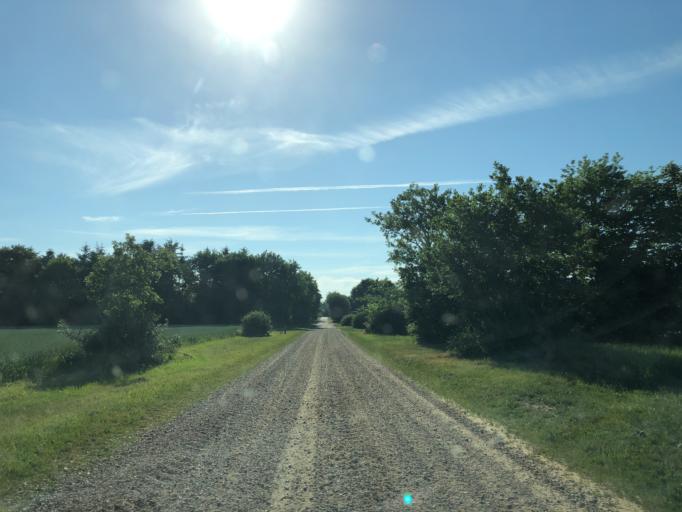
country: DK
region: Central Jutland
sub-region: Holstebro Kommune
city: Ulfborg
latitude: 56.3205
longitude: 8.3913
